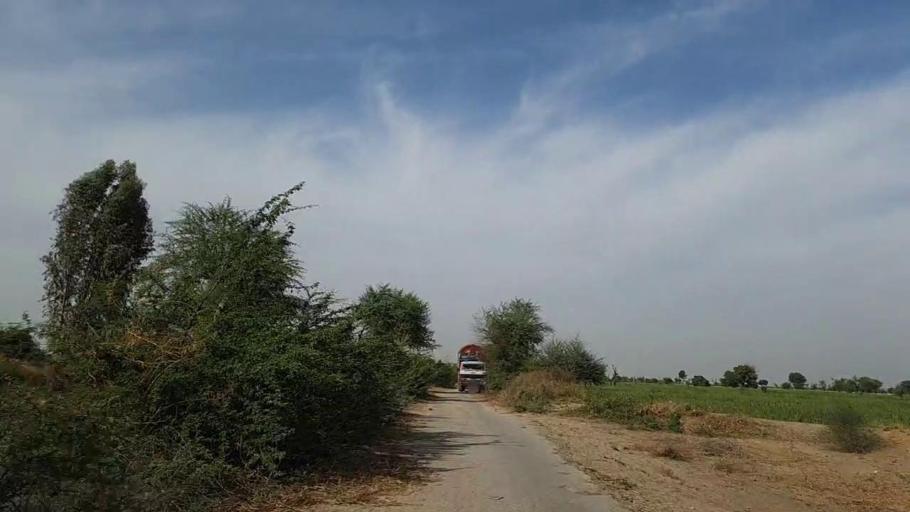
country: PK
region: Sindh
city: Samaro
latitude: 25.2393
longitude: 69.4238
